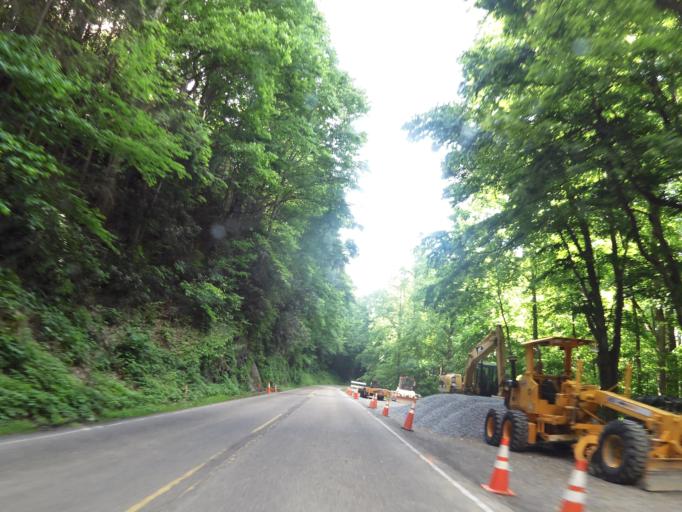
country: US
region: Tennessee
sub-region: Sevier County
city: Gatlinburg
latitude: 35.6440
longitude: -83.5080
